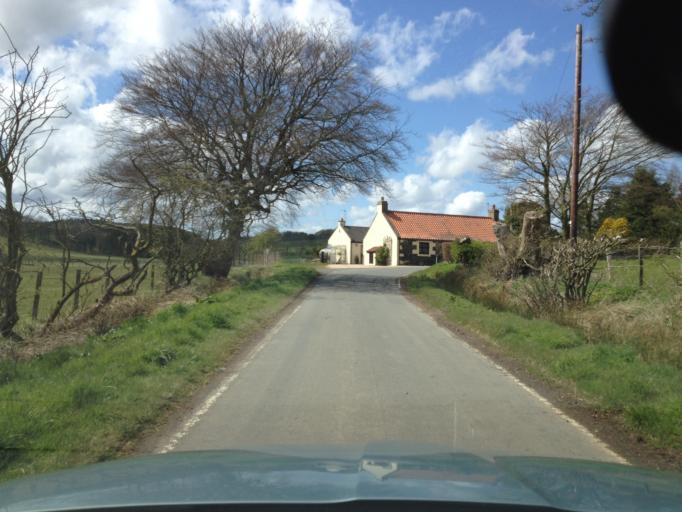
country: GB
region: Scotland
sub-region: West Lothian
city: Linlithgow
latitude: 55.9397
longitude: -3.5851
